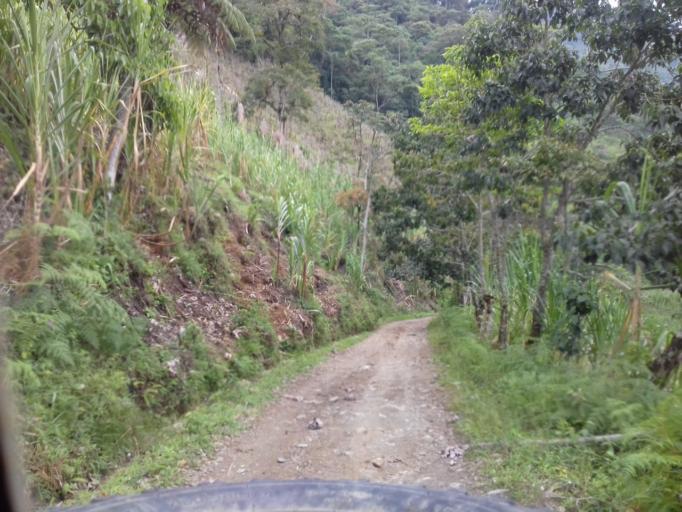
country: CO
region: Tolima
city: Libano
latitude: 4.9290
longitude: -75.0915
